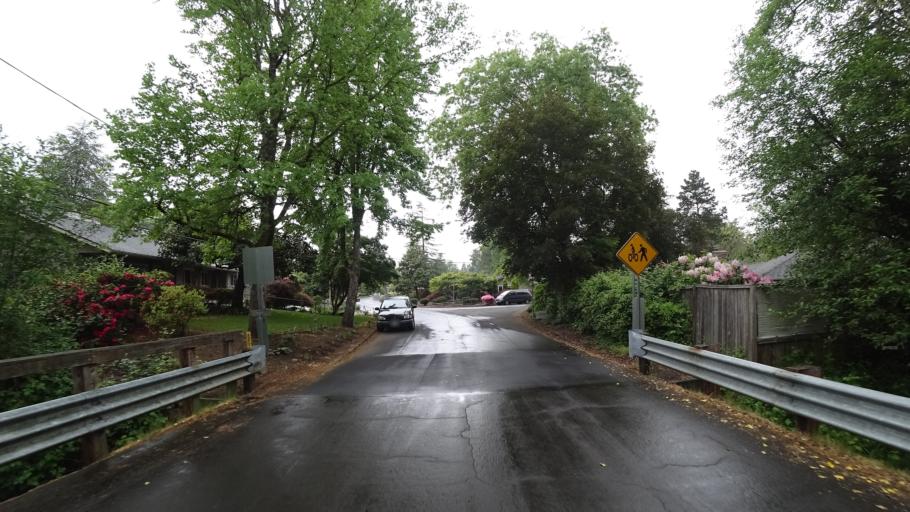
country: US
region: Oregon
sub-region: Washington County
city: Garden Home-Whitford
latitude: 45.4682
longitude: -122.7674
